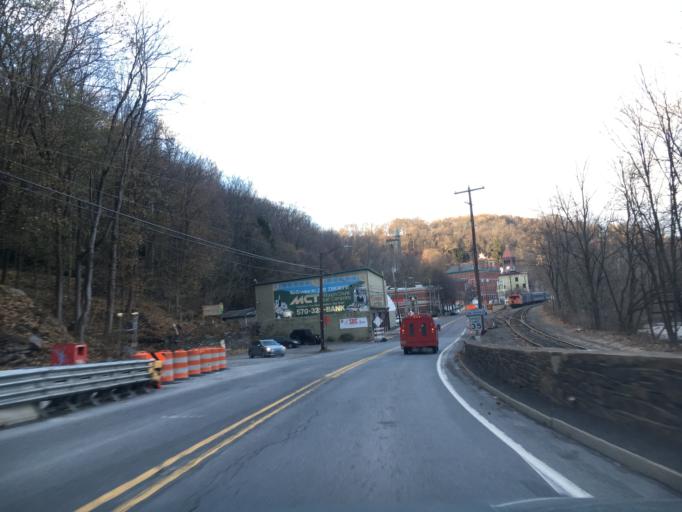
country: US
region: Pennsylvania
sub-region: Carbon County
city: Jim Thorpe
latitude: 40.8602
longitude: -75.7381
